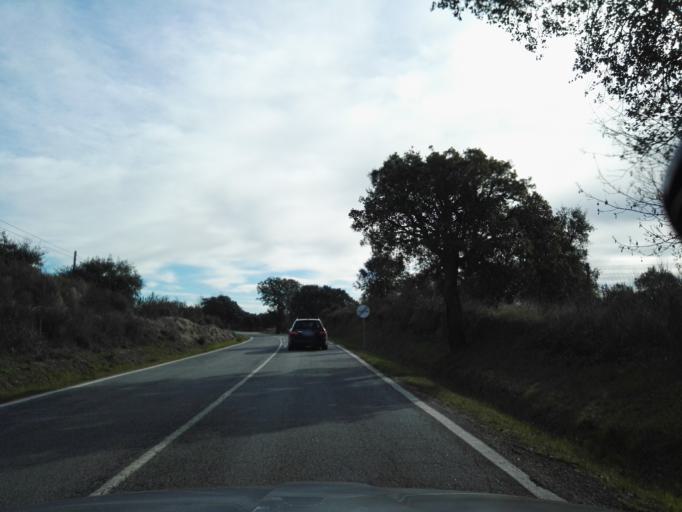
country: PT
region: Portalegre
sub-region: Nisa
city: Nisa
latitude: 39.5000
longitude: -7.6865
